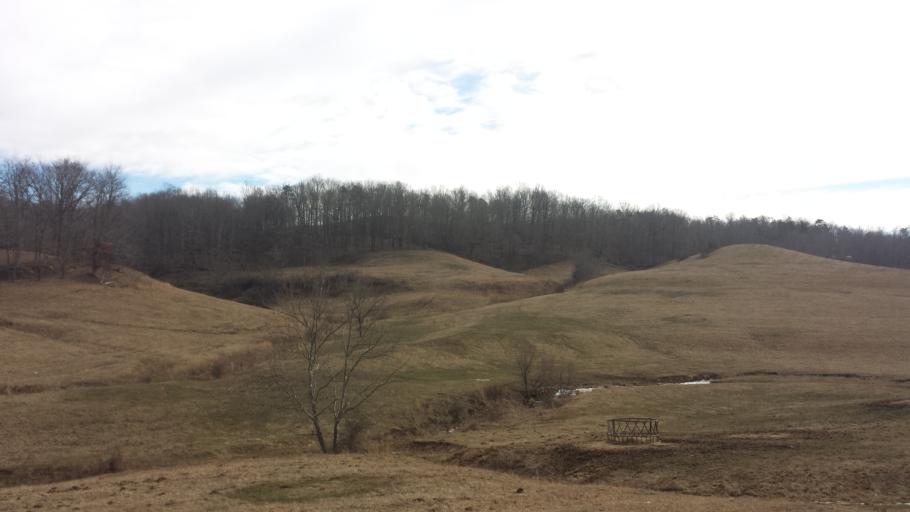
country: US
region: Ohio
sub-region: Gallia County
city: Gallipolis
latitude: 38.7606
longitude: -82.3549
